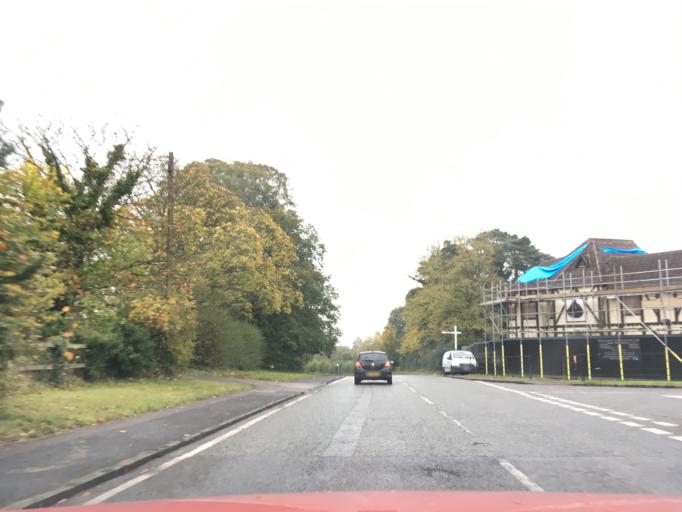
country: GB
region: England
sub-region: West Berkshire
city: Winterbourne
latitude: 51.4147
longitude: -1.3752
